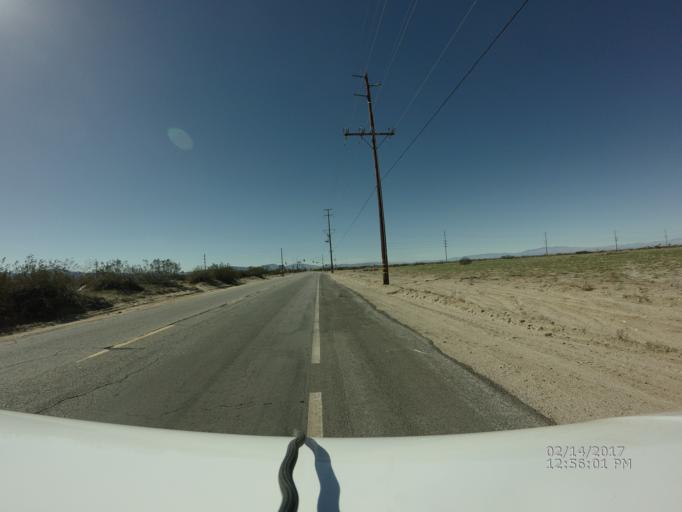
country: US
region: California
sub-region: Los Angeles County
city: Littlerock
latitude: 34.5800
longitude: -117.9322
